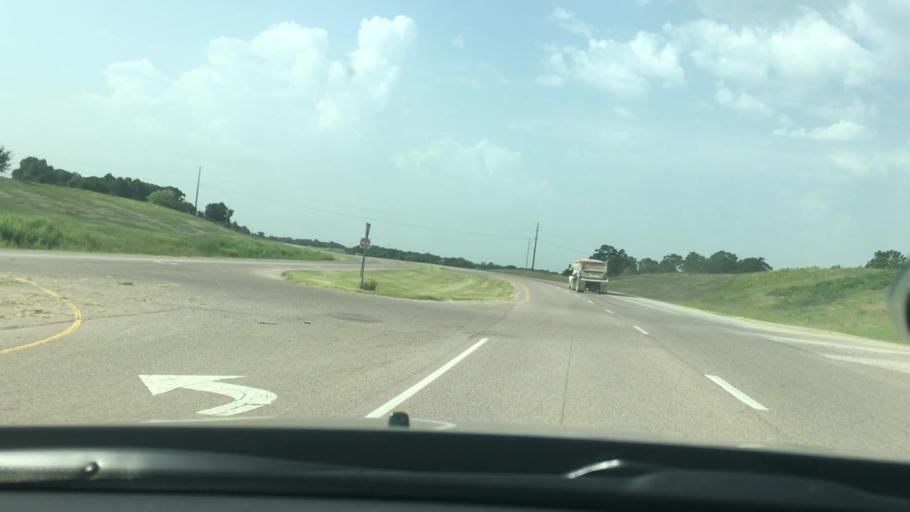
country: US
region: Oklahoma
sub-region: Pontotoc County
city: Byng
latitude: 34.8291
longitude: -96.6936
